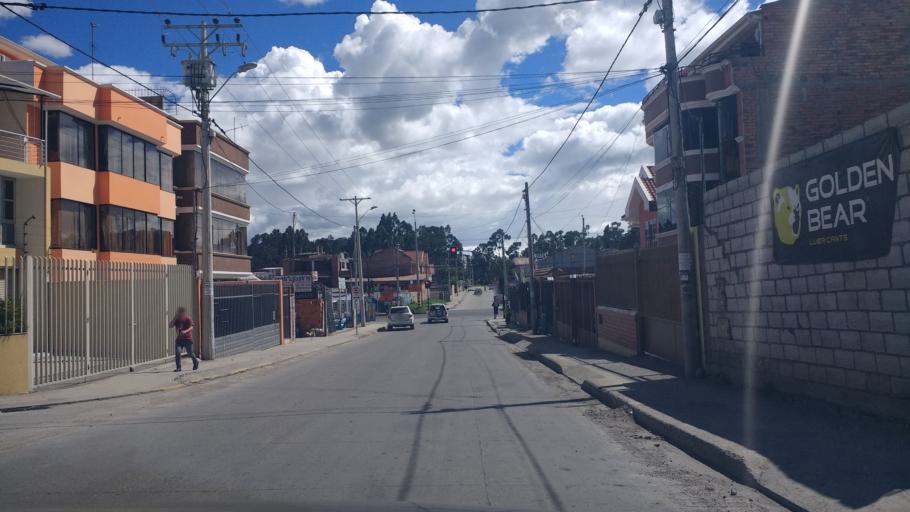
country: EC
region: Azuay
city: Cuenca
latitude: -2.9023
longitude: -79.0349
